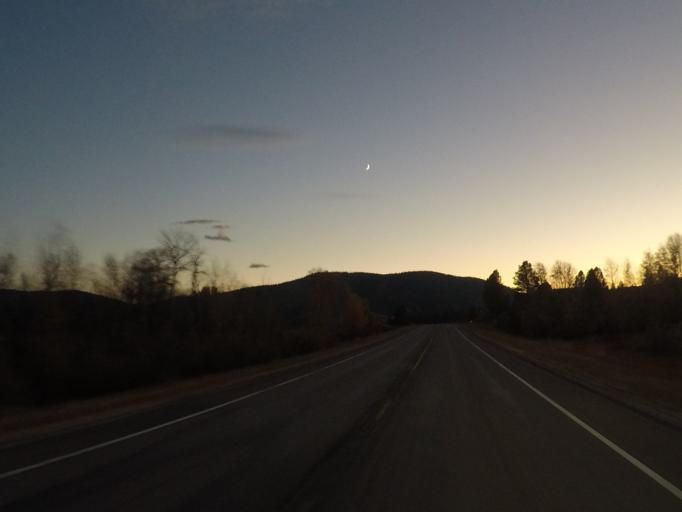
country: US
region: Montana
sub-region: Missoula County
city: Seeley Lake
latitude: 47.0371
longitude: -113.2281
